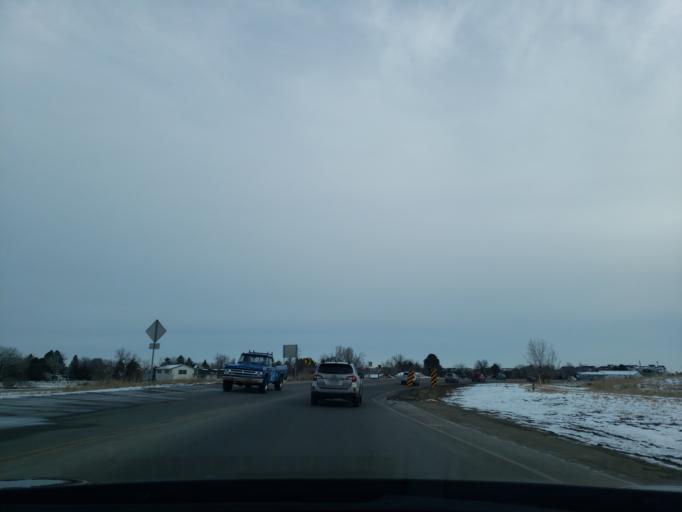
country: US
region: Colorado
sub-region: Larimer County
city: Campion
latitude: 40.3463
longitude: -105.0945
